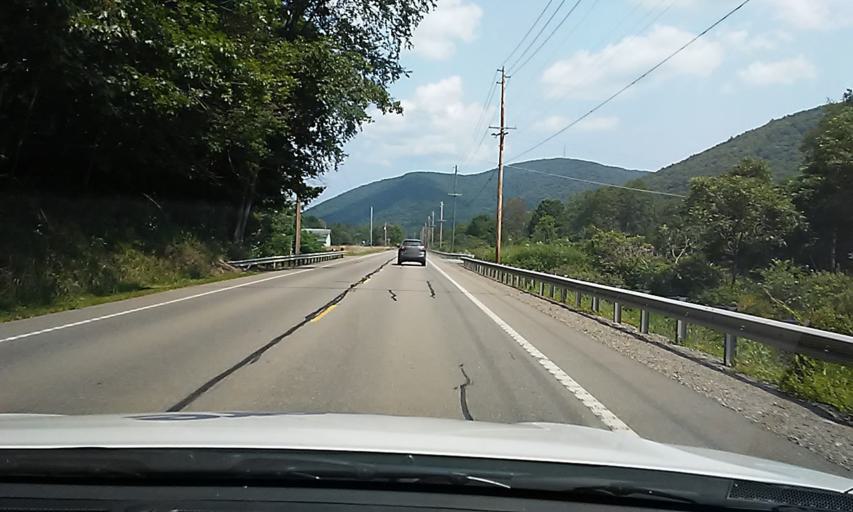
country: US
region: Pennsylvania
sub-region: Cameron County
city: Emporium
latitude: 41.4917
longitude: -78.2893
